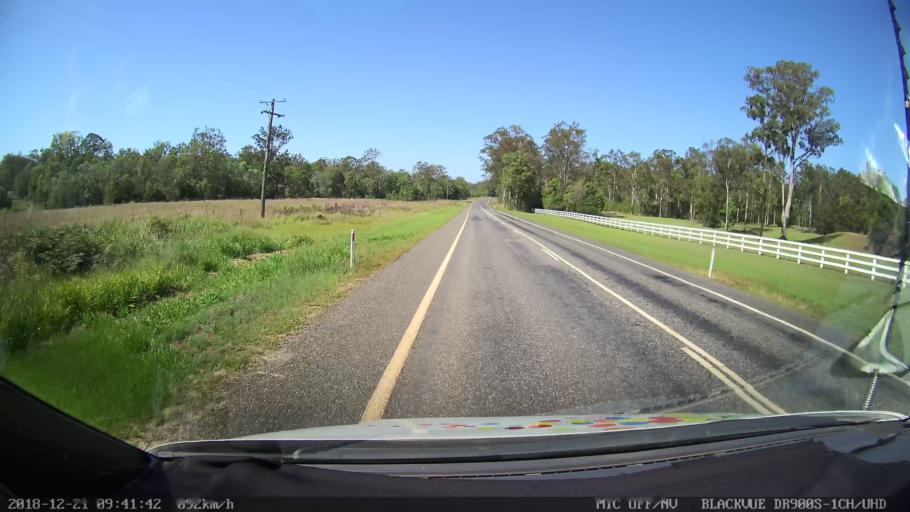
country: AU
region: New South Wales
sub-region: Clarence Valley
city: Grafton
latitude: -29.5882
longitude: 152.9544
